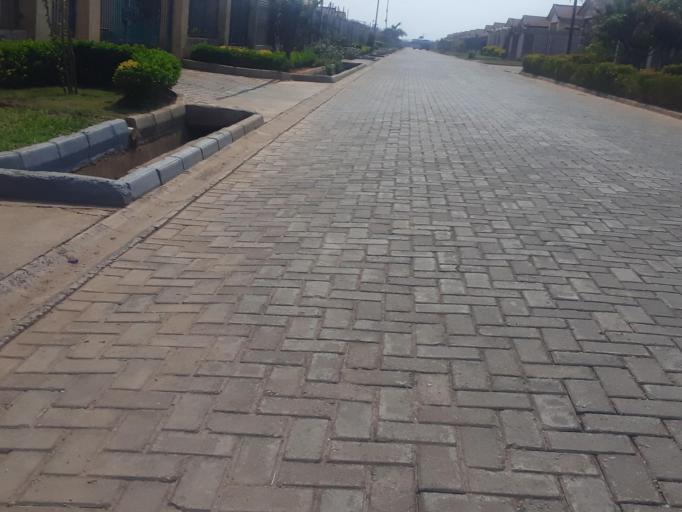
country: ZM
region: Lusaka
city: Lusaka
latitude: -15.3598
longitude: 28.2795
